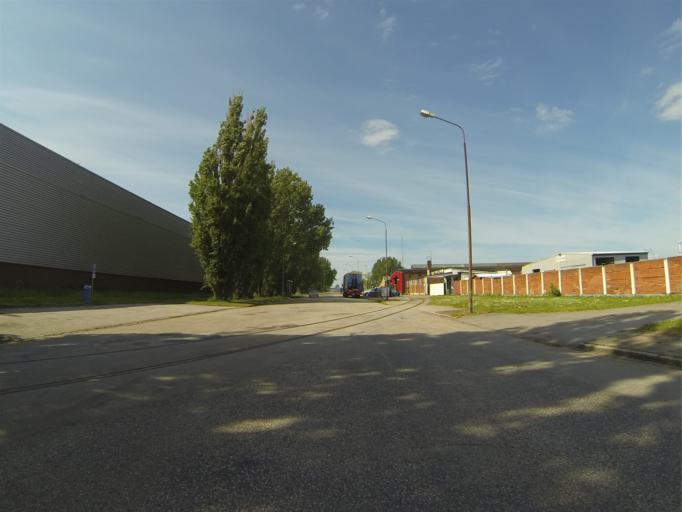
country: SE
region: Skane
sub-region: Malmo
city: Malmoe
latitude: 55.6173
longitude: 13.0271
